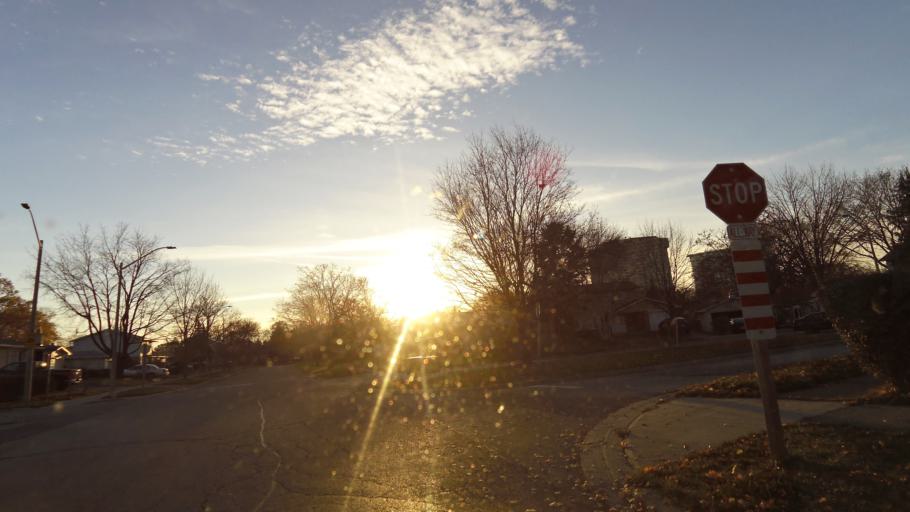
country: CA
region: Ontario
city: Etobicoke
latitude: 43.6159
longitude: -79.5900
